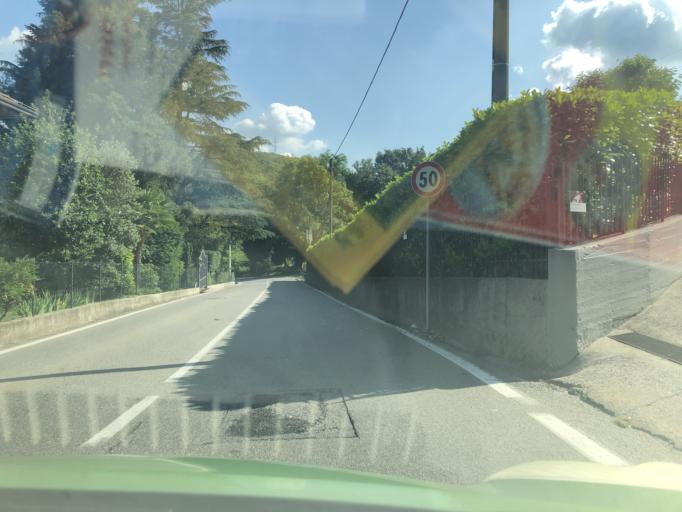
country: IT
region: Piedmont
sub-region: Provincia di Novara
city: Meina
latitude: 45.7760
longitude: 8.5366
